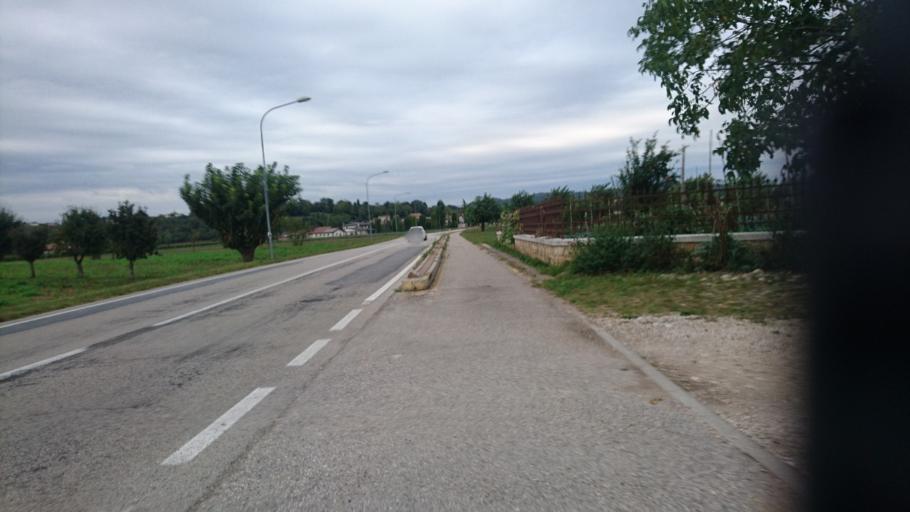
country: IT
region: Veneto
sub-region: Provincia di Vicenza
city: Tavernelle
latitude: 45.5158
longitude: 11.4305
